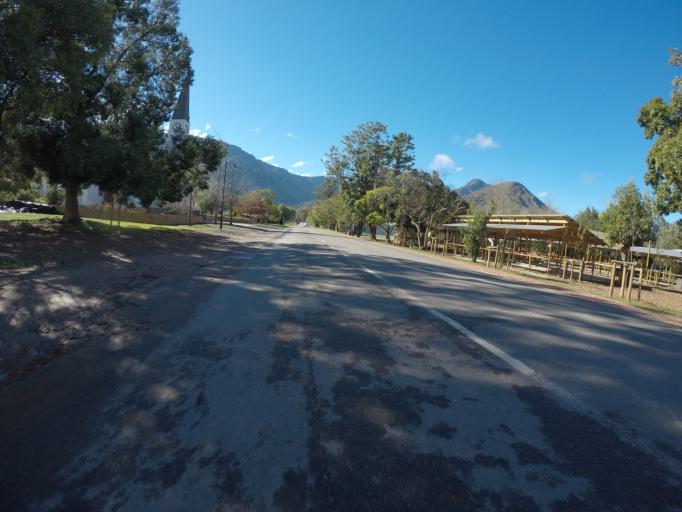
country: ZA
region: Western Cape
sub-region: Overberg District Municipality
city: Caledon
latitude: -34.0490
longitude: 19.6094
